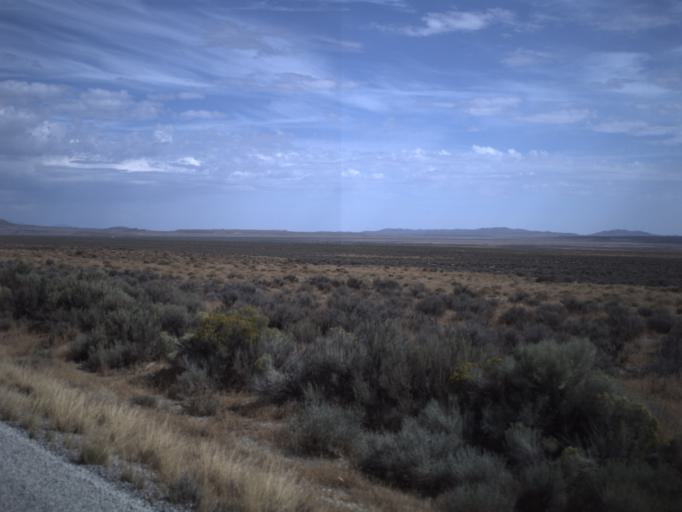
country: US
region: Utah
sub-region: Tooele County
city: Wendover
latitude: 41.5236
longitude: -113.5963
